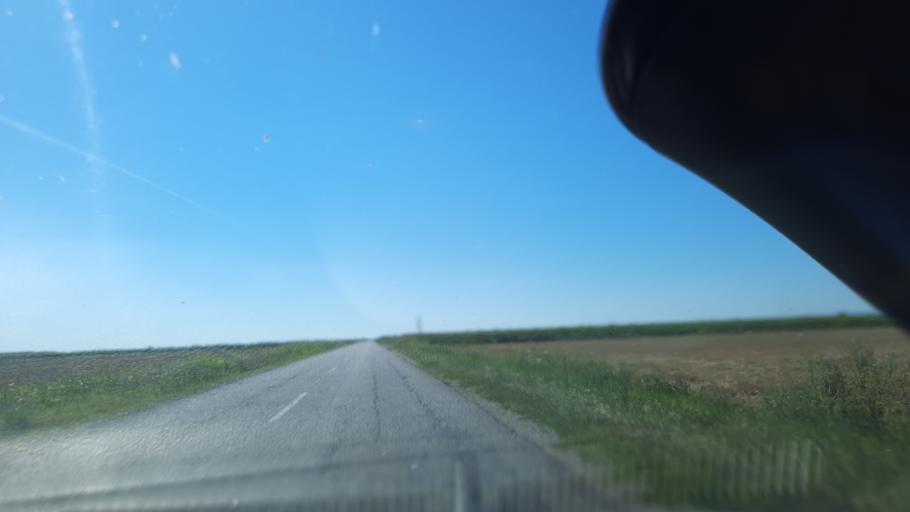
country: RS
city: Simanovci
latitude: 44.8787
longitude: 20.0609
